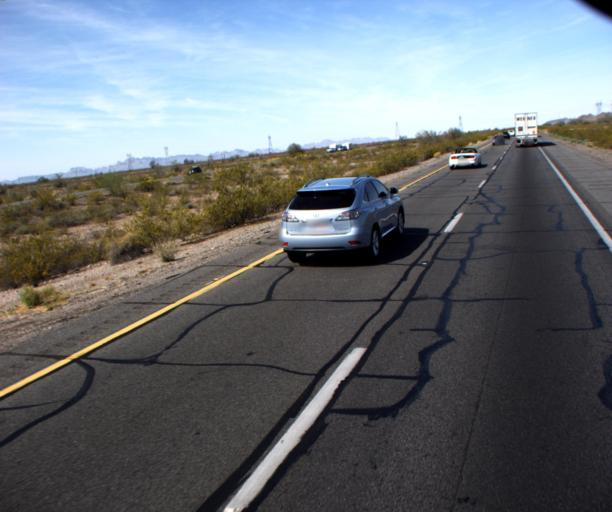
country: US
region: Arizona
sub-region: Maricopa County
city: Buckeye
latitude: 33.5119
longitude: -113.0168
